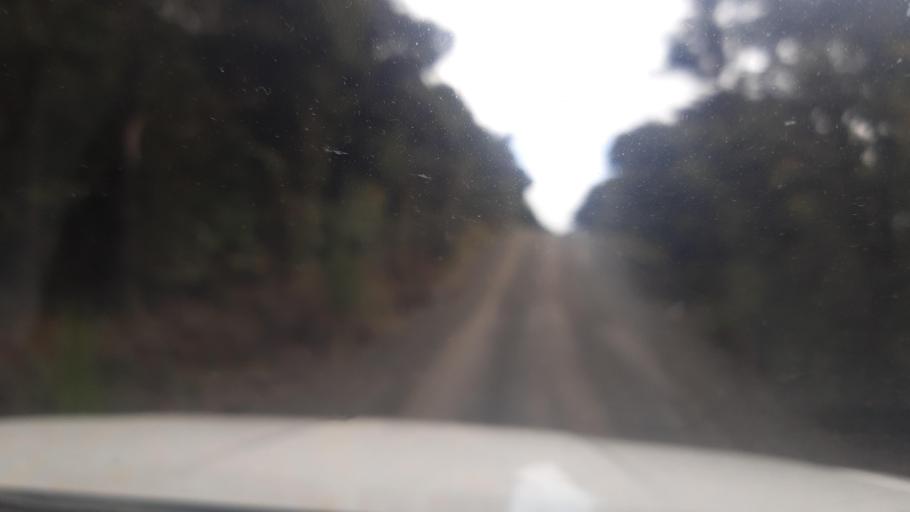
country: NZ
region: Northland
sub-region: Far North District
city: Taipa
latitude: -35.0589
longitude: 173.5344
